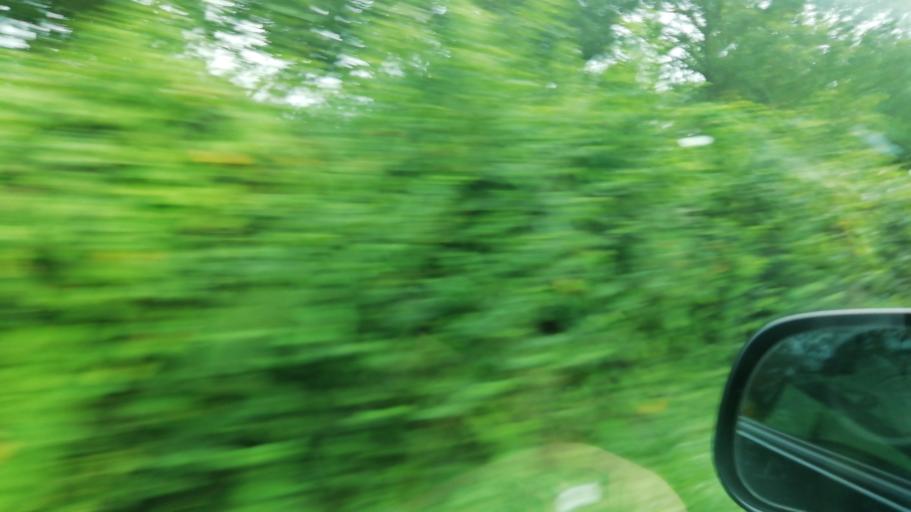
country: IE
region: Munster
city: Fethard
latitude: 52.4828
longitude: -7.6933
